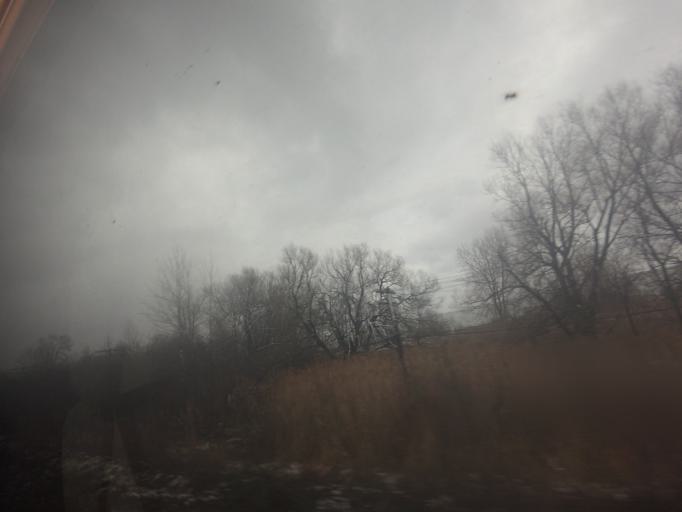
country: CA
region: Ontario
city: Cobourg
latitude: 43.9539
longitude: -78.2459
